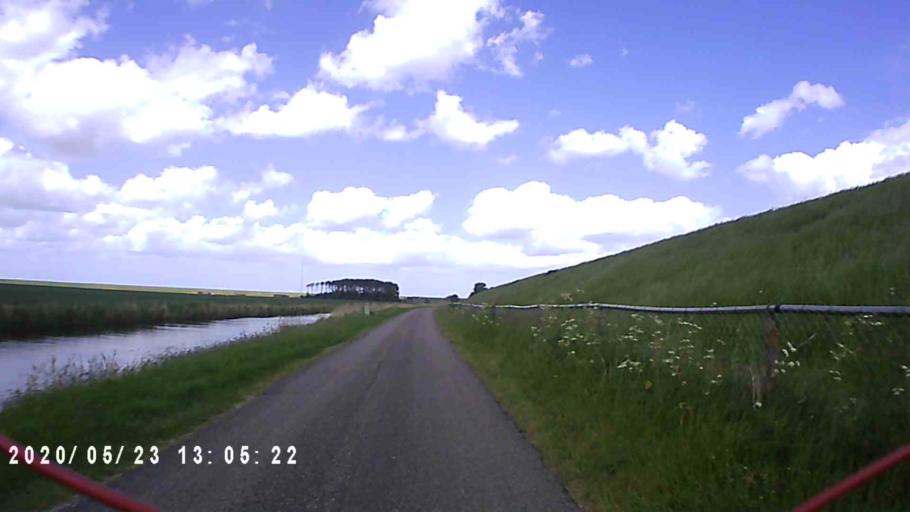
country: DE
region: Lower Saxony
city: Emden
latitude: 53.2928
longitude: 7.0756
